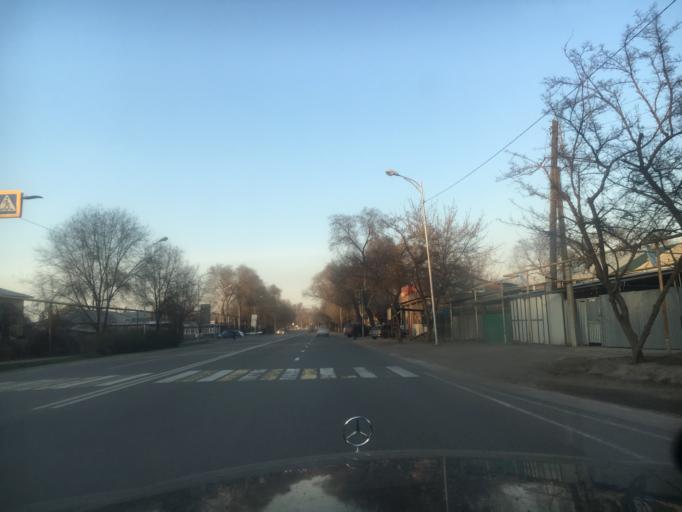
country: KZ
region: Almaty Oblysy
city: Pervomayskiy
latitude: 43.3579
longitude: 76.9790
